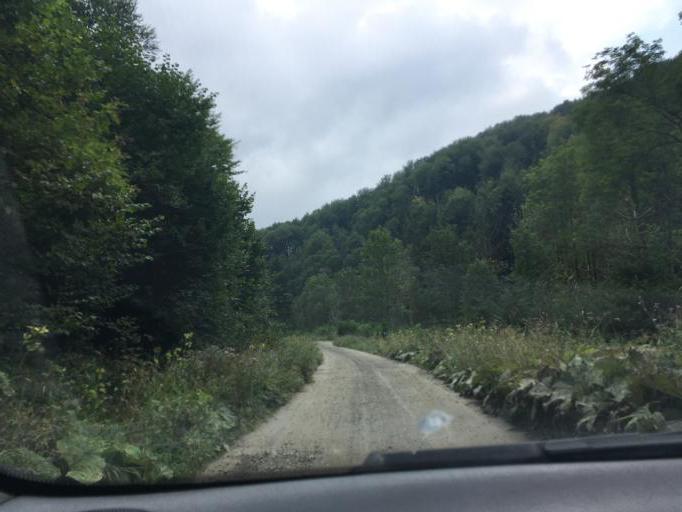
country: PL
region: Subcarpathian Voivodeship
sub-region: Powiat bieszczadzki
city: Lutowiska
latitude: 49.1885
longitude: 22.6151
